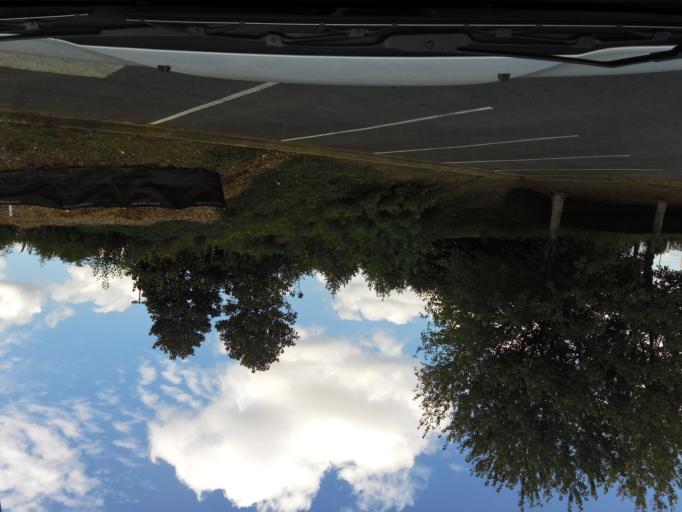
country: US
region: Georgia
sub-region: Cobb County
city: Kennesaw
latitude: 34.0057
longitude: -84.5736
